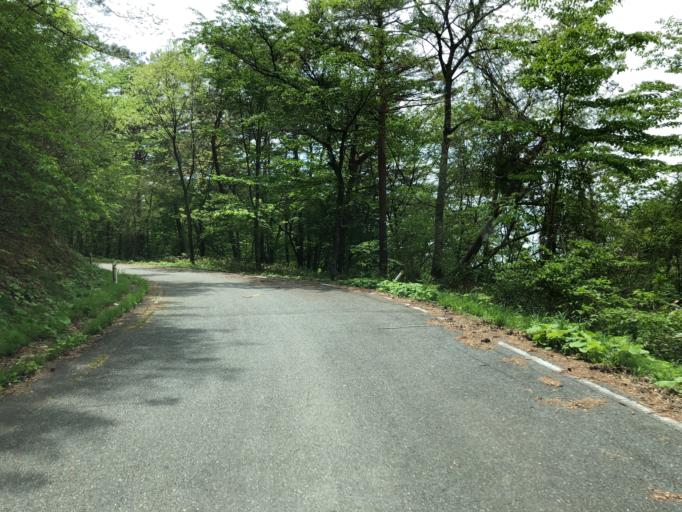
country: JP
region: Miyagi
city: Marumori
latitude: 37.7105
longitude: 140.7809
